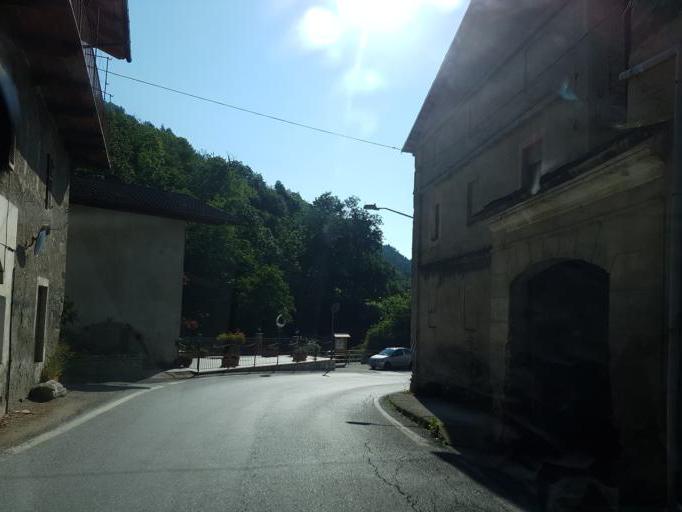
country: IT
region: Piedmont
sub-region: Provincia di Cuneo
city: San Damiano Macra
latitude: 44.4871
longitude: 7.2689
